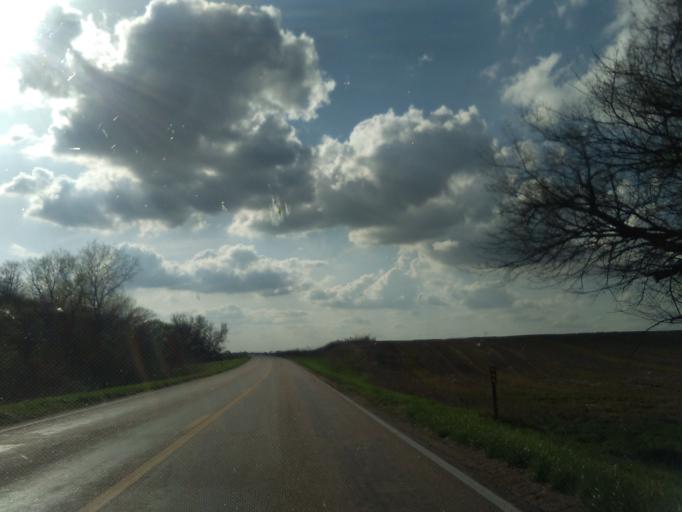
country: US
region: Nebraska
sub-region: Webster County
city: Red Cloud
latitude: 40.0913
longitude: -98.6184
